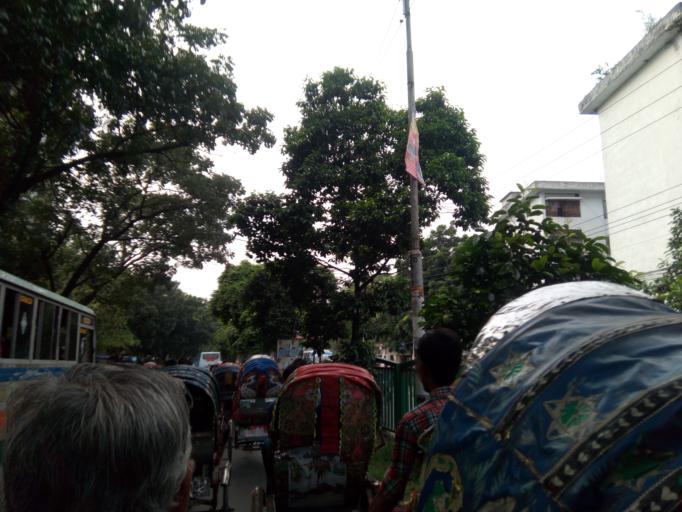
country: BD
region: Dhaka
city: Azimpur
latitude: 23.7252
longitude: 90.3868
